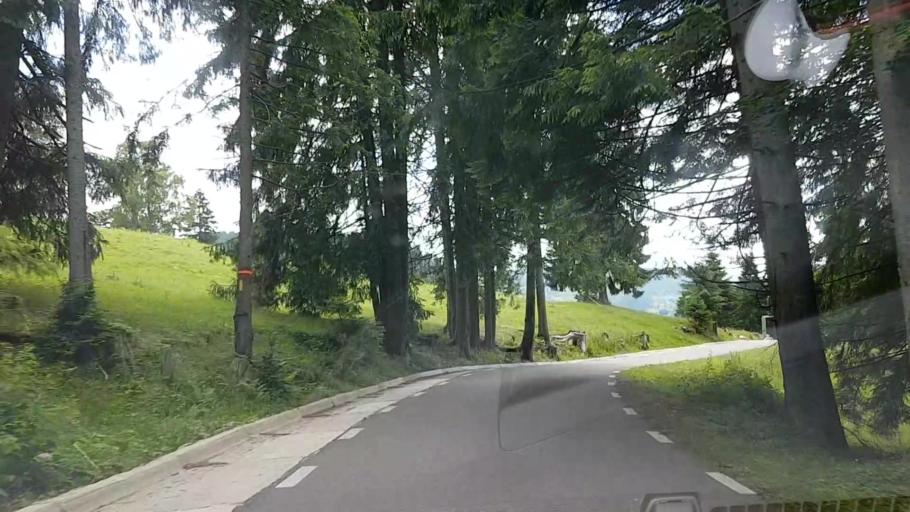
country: RO
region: Suceava
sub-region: Comuna Crucea
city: Crucea
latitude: 47.4296
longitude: 25.5739
